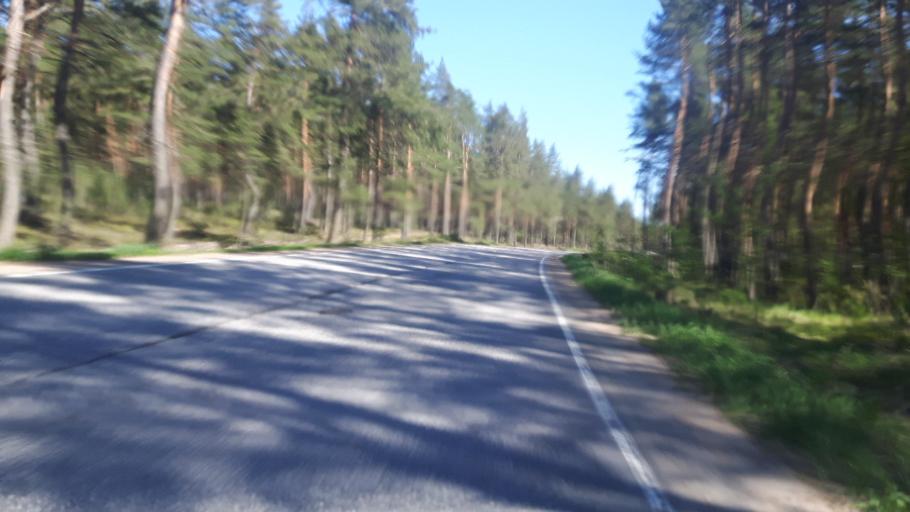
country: RU
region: Leningrad
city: Glebychevo
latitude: 60.2760
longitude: 28.9275
